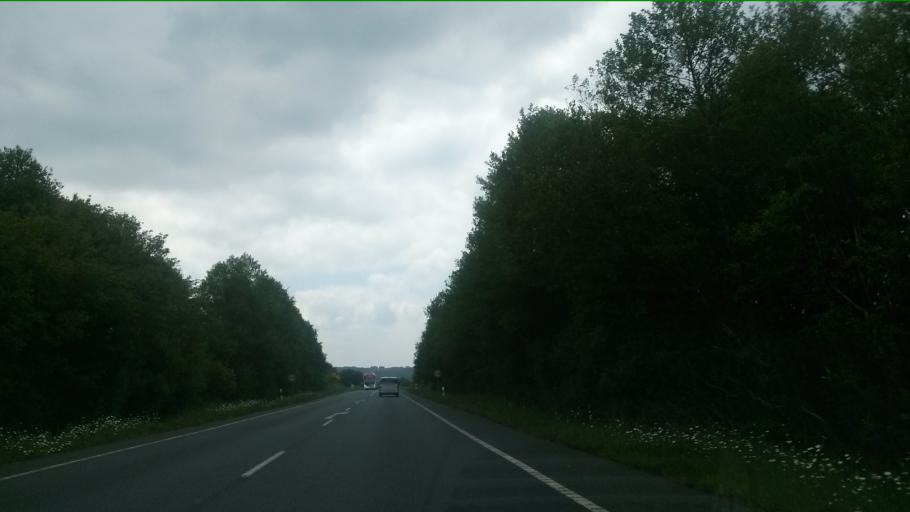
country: ES
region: Galicia
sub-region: Provincia da Coruna
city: Curtis
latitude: 43.1191
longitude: -8.0910
